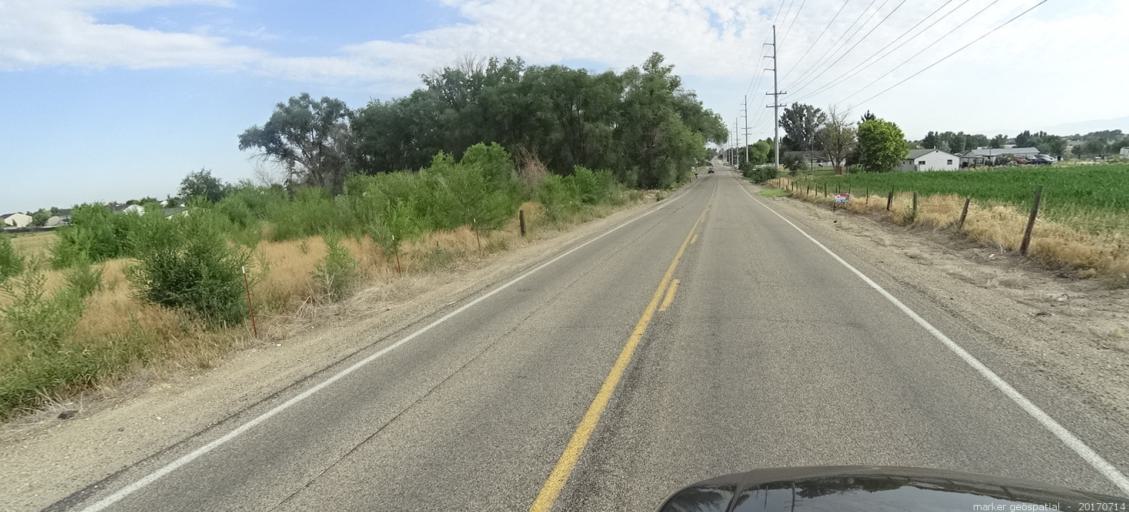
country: US
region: Idaho
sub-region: Ada County
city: Kuna
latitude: 43.4762
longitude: -116.4137
